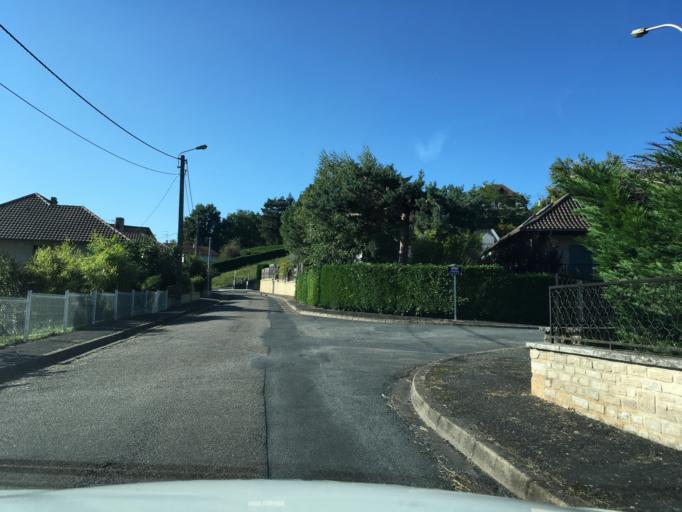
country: FR
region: Limousin
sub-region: Departement de la Correze
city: Malemort-sur-Correze
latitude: 45.1731
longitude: 1.5495
